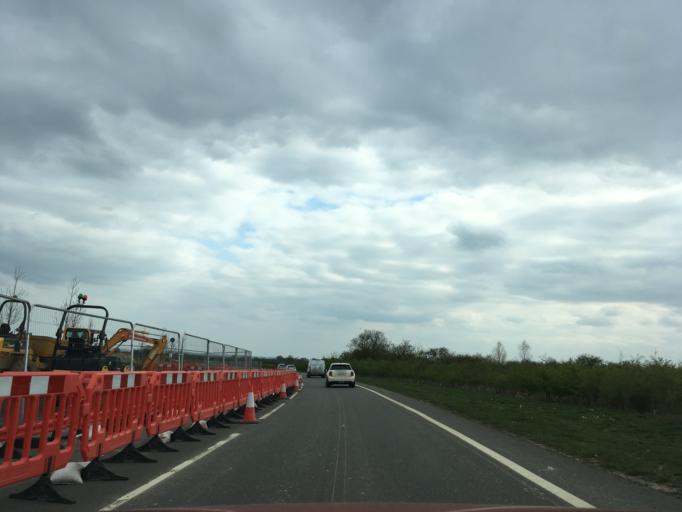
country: GB
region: England
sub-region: Oxfordshire
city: Bicester
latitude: 51.8965
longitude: -1.1831
